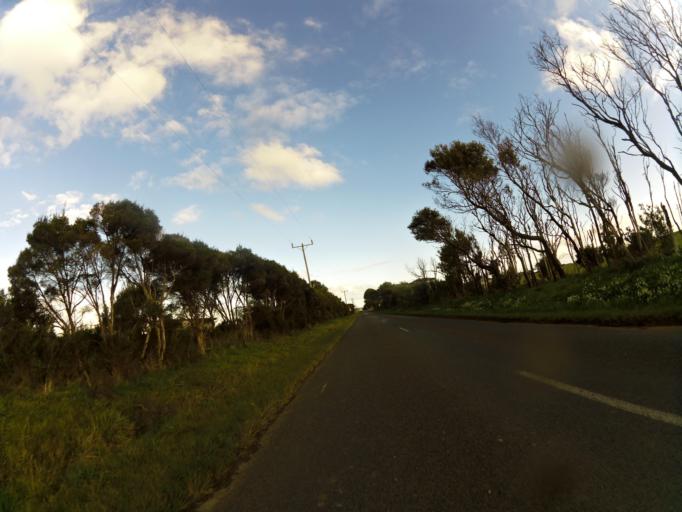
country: AU
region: Victoria
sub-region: Bass Coast
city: North Wonthaggi
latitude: -38.5553
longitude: 145.5491
